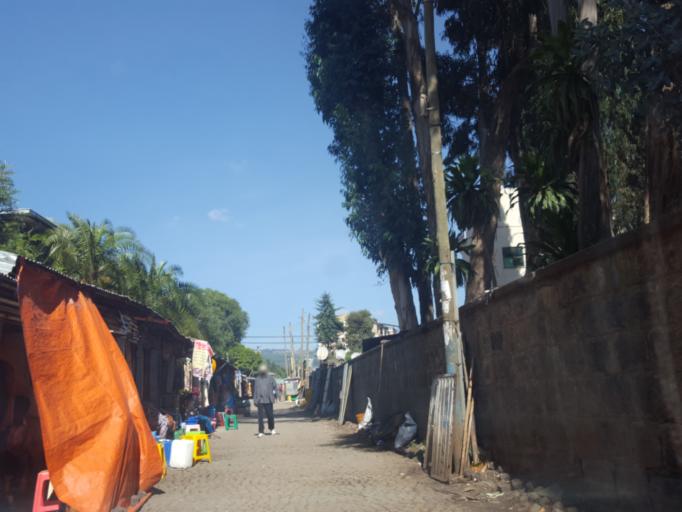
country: ET
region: Adis Abeba
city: Addis Ababa
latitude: 9.0541
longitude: 38.7428
